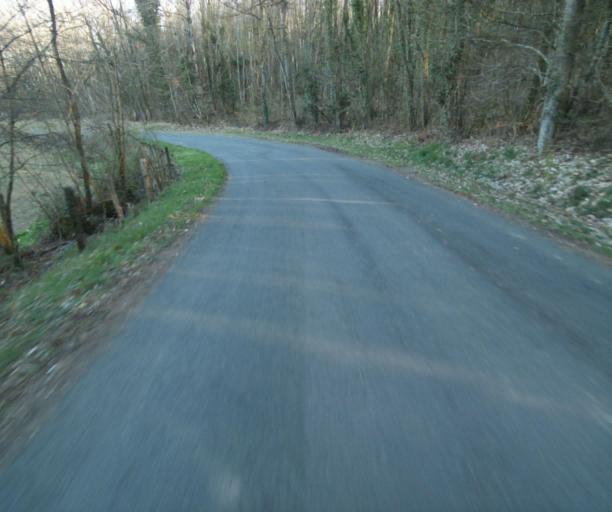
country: FR
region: Limousin
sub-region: Departement de la Correze
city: Seilhac
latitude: 45.3597
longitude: 1.7064
